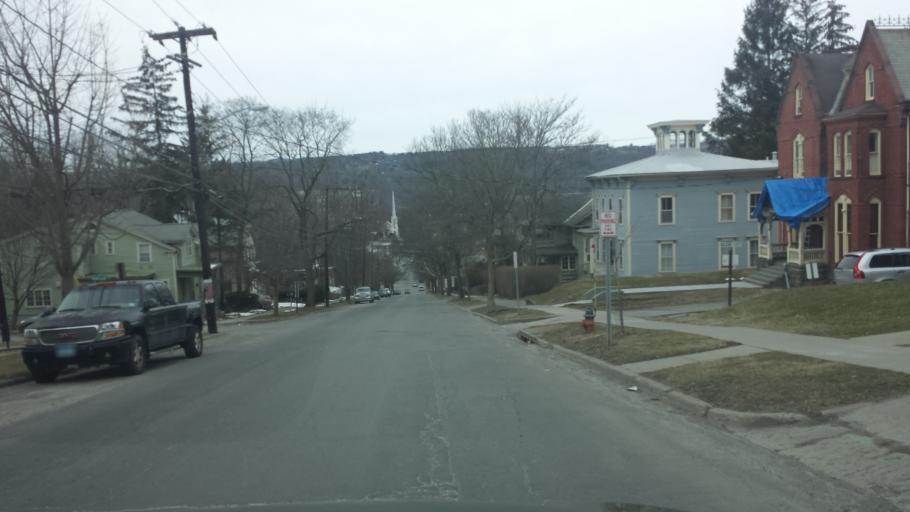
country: US
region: New York
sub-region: Tompkins County
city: Ithaca
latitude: 42.4416
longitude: -76.4917
